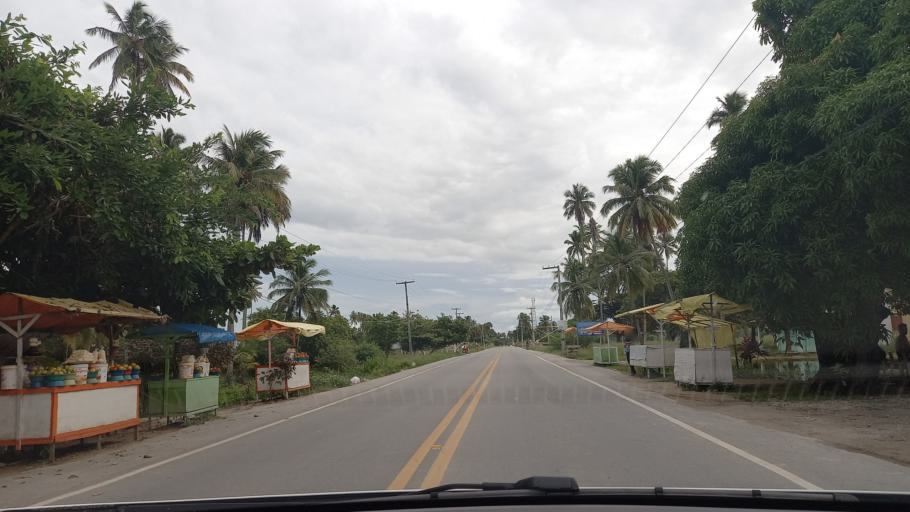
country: BR
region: Pernambuco
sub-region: Sao Jose Da Coroa Grande
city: Sao Jose da Coroa Grande
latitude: -8.9206
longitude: -35.1571
